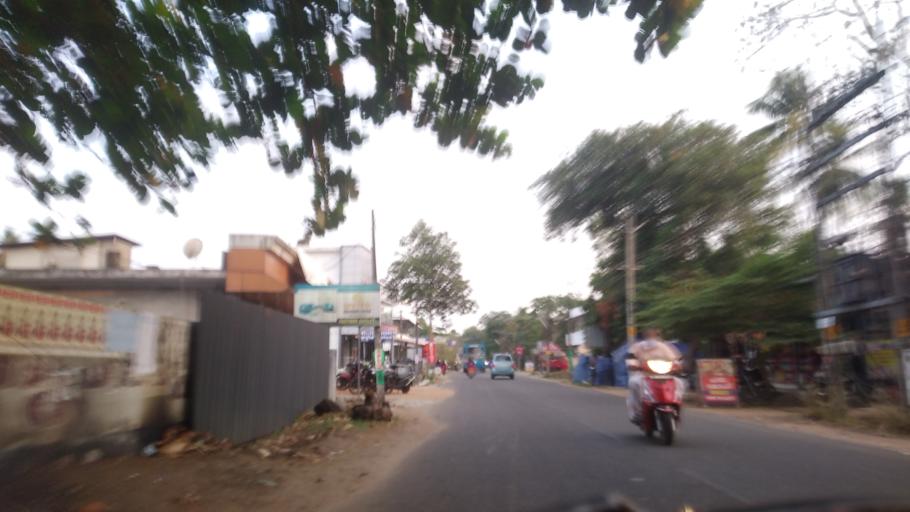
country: IN
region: Kerala
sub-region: Thrissur District
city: Kodungallur
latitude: 10.2172
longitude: 76.1601
